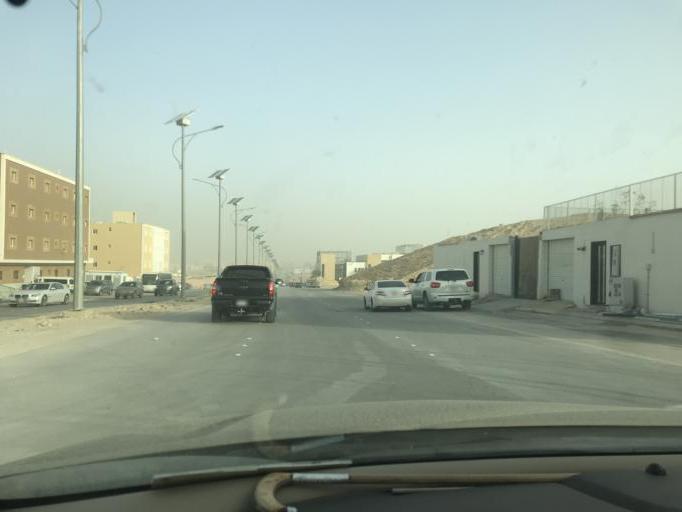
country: SA
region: Ar Riyad
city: Riyadh
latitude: 24.8398
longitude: 46.6673
